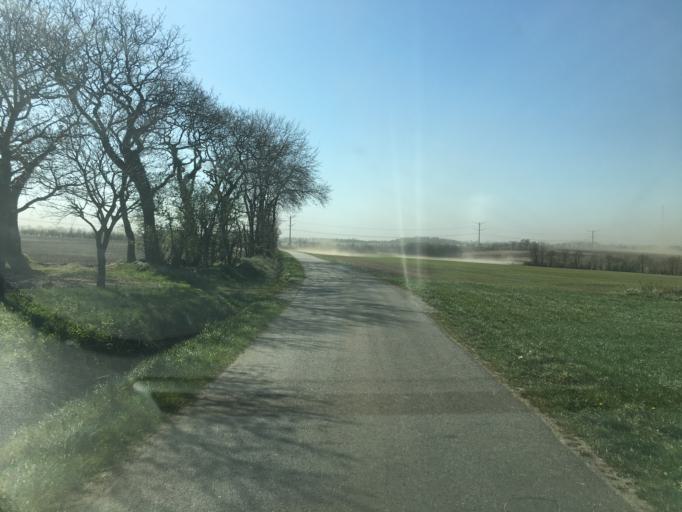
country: DK
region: South Denmark
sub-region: Aabenraa Kommune
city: Rodekro
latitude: 55.1067
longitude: 9.2284
